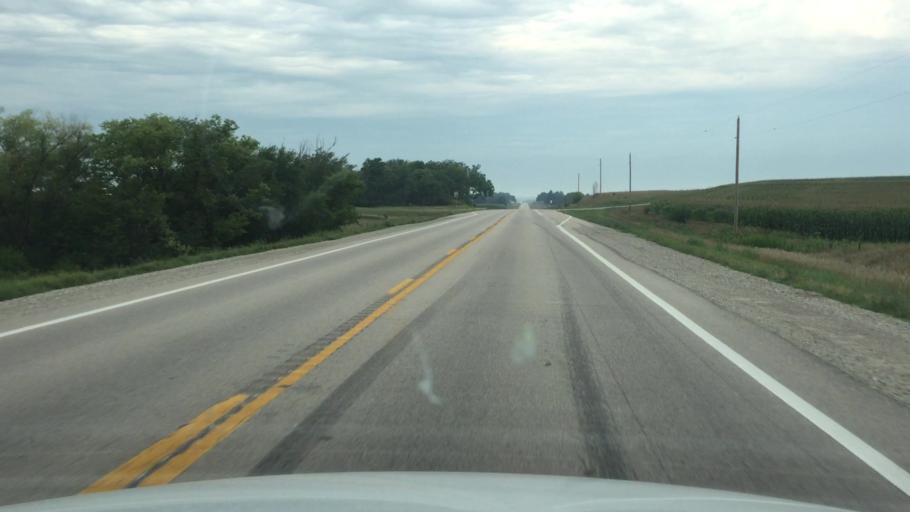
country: US
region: Kansas
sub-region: Brown County
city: Hiawatha
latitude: 39.8486
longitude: -95.5984
